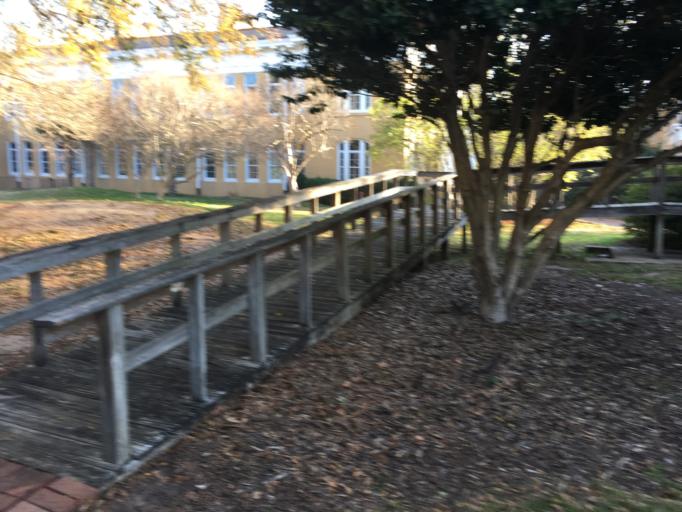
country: US
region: South Carolina
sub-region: Richland County
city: Columbia
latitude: 33.9976
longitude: -81.0266
